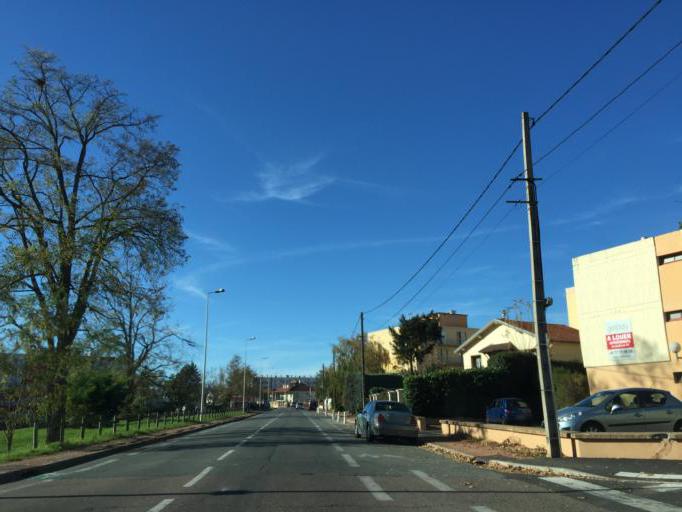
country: FR
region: Rhone-Alpes
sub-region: Departement de la Loire
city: Riorges
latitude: 46.0337
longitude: 4.0550
